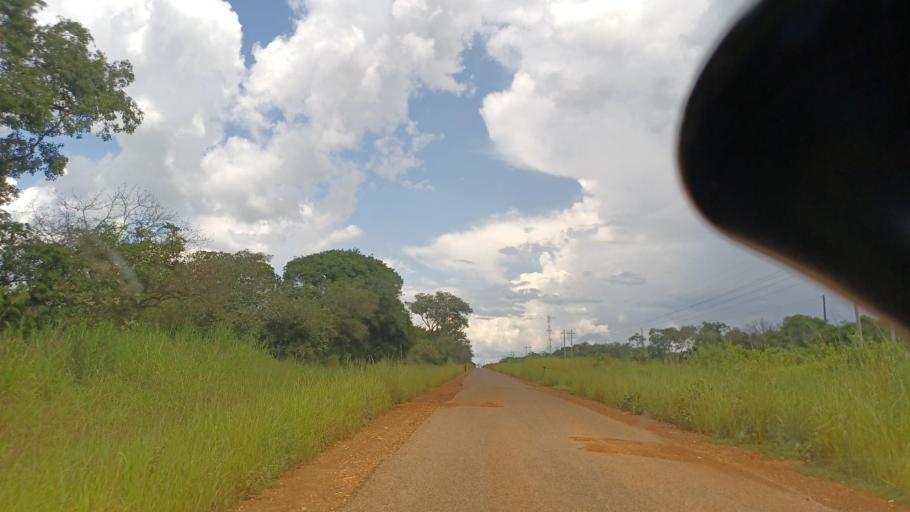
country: ZM
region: North-Western
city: Kasempa
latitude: -12.7902
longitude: 26.0136
